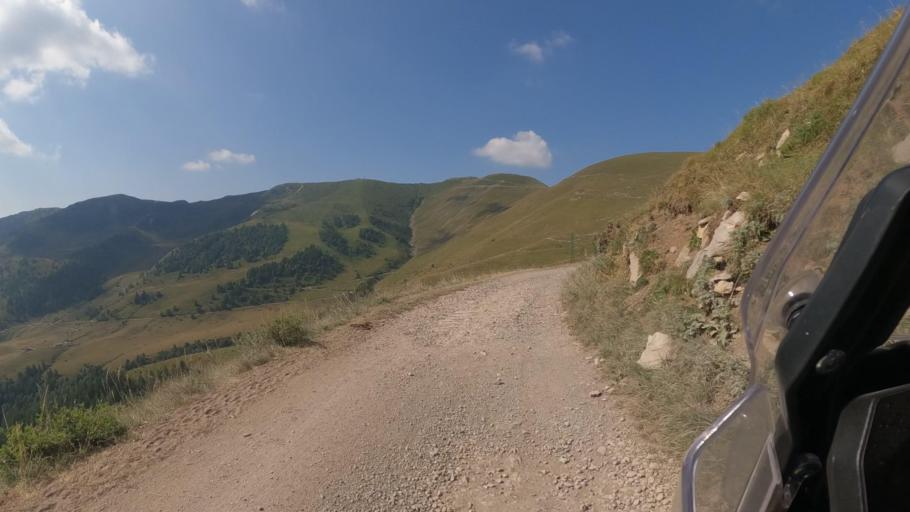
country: IT
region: Piedmont
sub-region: Provincia di Cuneo
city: Briga Alta
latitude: 44.0795
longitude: 7.7259
